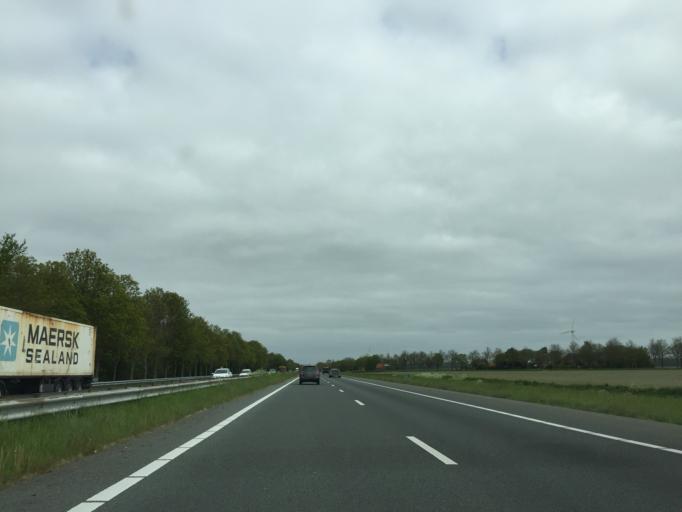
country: NL
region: North Holland
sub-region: Gemeente Hollands Kroon
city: Den Oever
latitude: 52.8758
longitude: 5.0235
